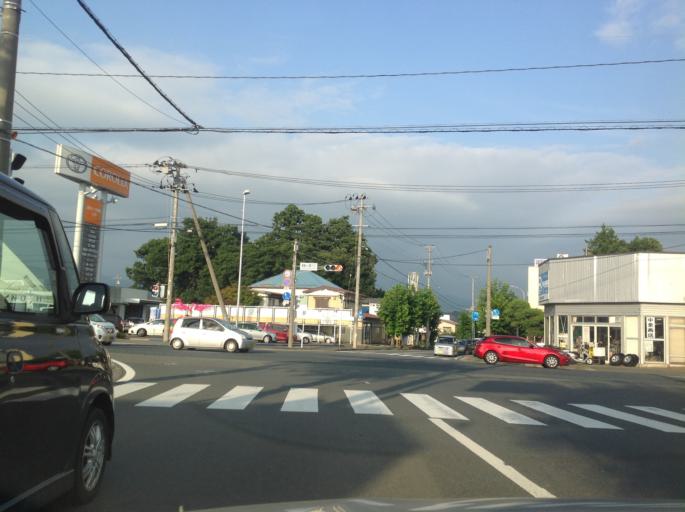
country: JP
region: Iwate
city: Morioka-shi
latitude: 39.5525
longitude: 141.1668
